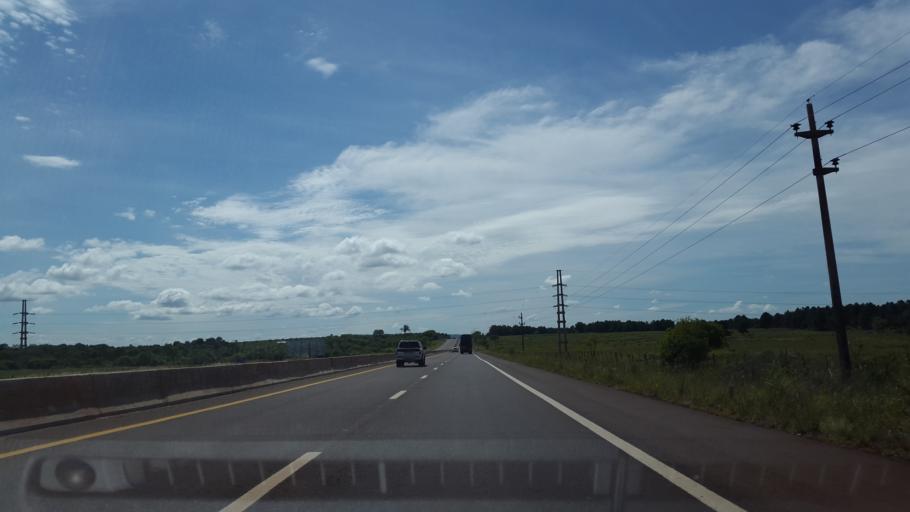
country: AR
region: Misiones
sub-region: Departamento de Candelaria
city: Candelaria
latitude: -27.4626
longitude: -55.6996
